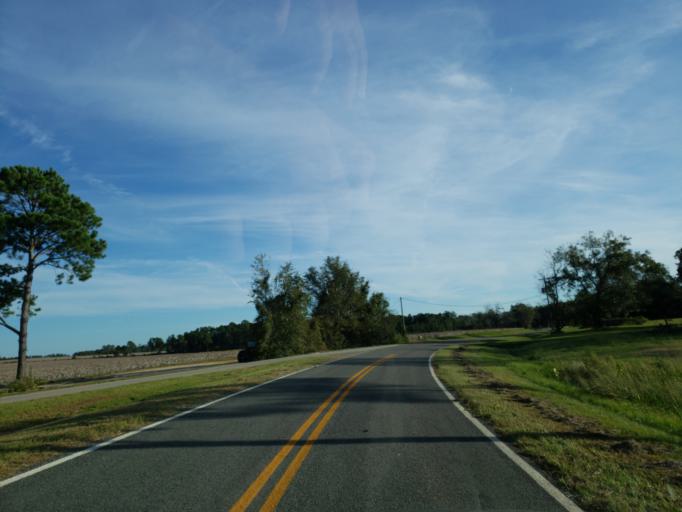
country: US
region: Georgia
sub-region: Dooly County
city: Vienna
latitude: 32.0580
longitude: -83.7616
